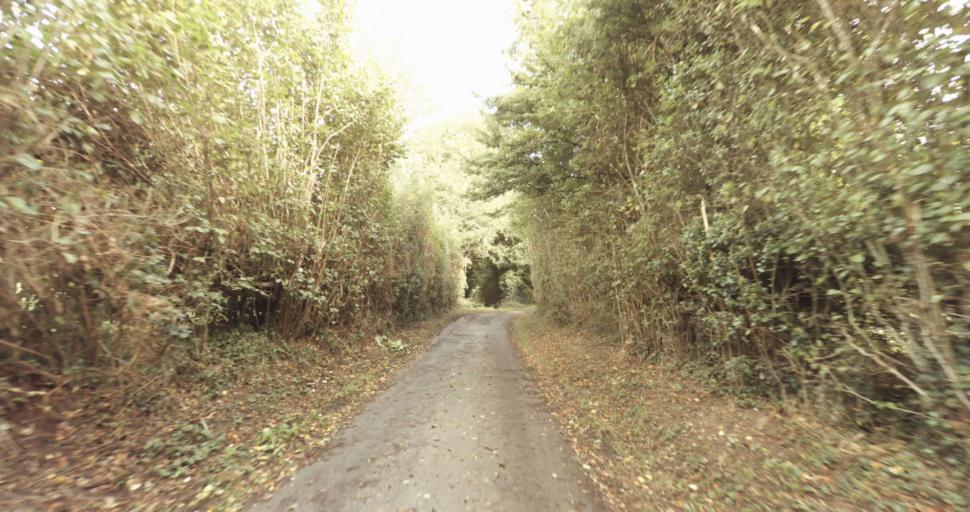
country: FR
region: Lower Normandy
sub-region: Departement de l'Orne
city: Sainte-Gauburge-Sainte-Colombe
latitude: 48.7048
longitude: 0.3717
